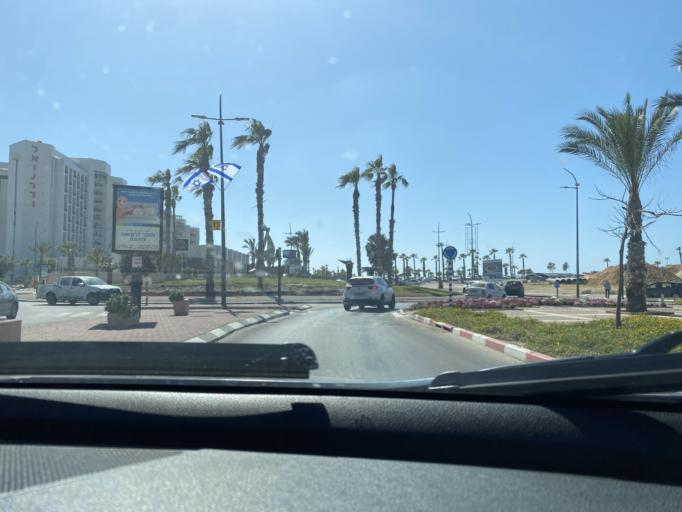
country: IL
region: Southern District
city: Ashqelon
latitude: 31.6839
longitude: 34.5633
